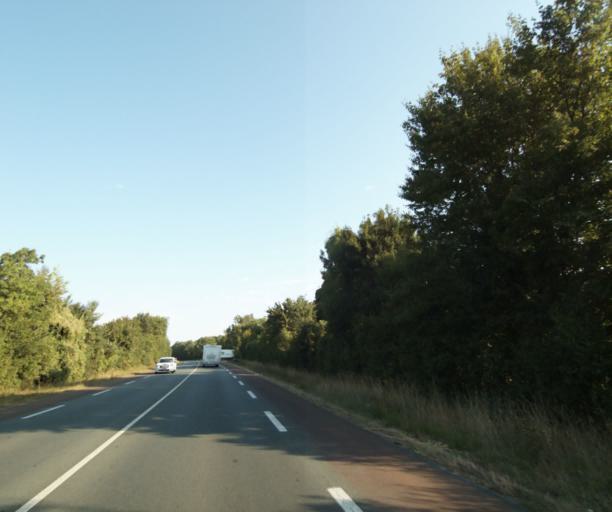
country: FR
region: Poitou-Charentes
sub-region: Departement de la Charente-Maritime
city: Cabariot
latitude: 45.9433
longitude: -0.8644
